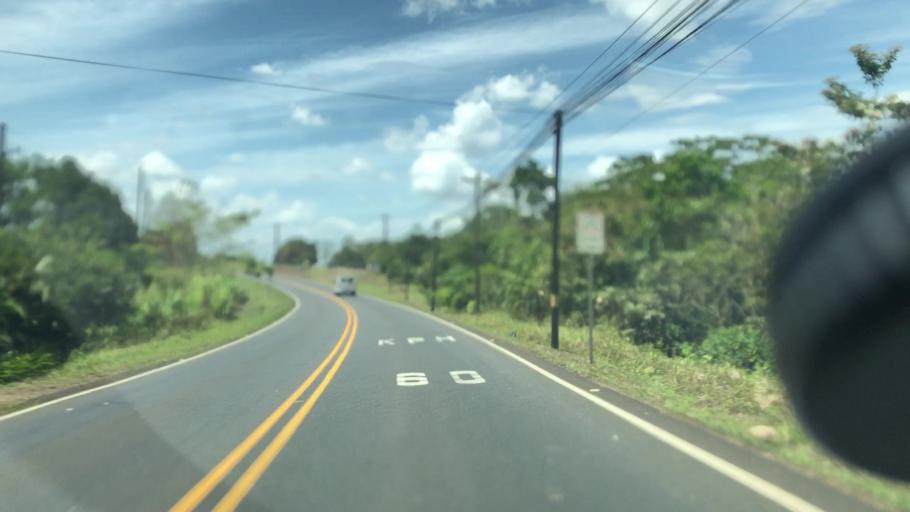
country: CR
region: Alajuela
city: Pital
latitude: 10.4582
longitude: -84.3890
